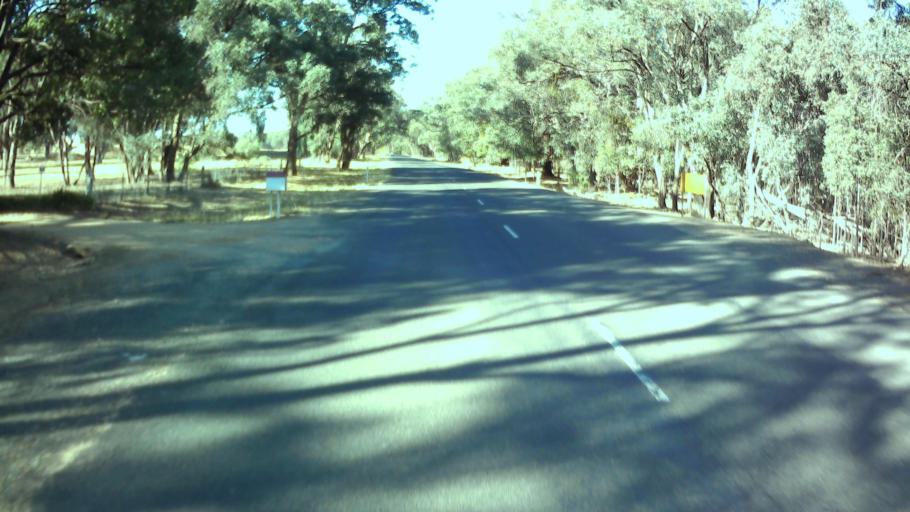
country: AU
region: New South Wales
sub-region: Weddin
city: Grenfell
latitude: -33.9905
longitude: 148.1371
